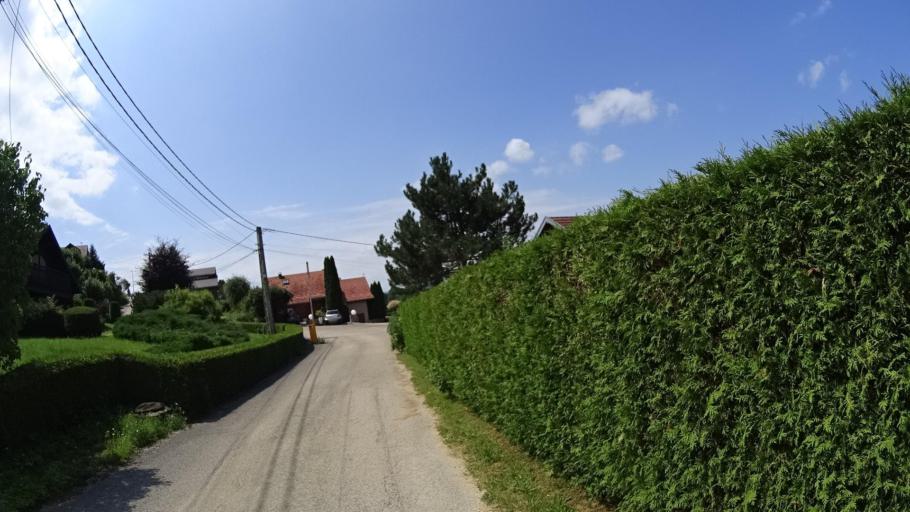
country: FR
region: Franche-Comte
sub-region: Departement du Doubs
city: Les Fourgs
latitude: 46.8187
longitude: 6.3249
